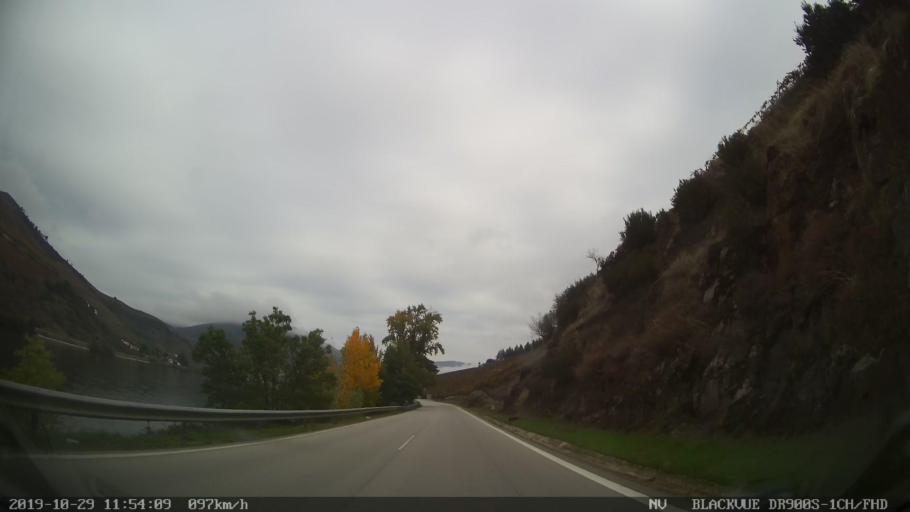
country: PT
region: Viseu
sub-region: Armamar
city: Armamar
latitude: 41.1430
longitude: -7.6904
